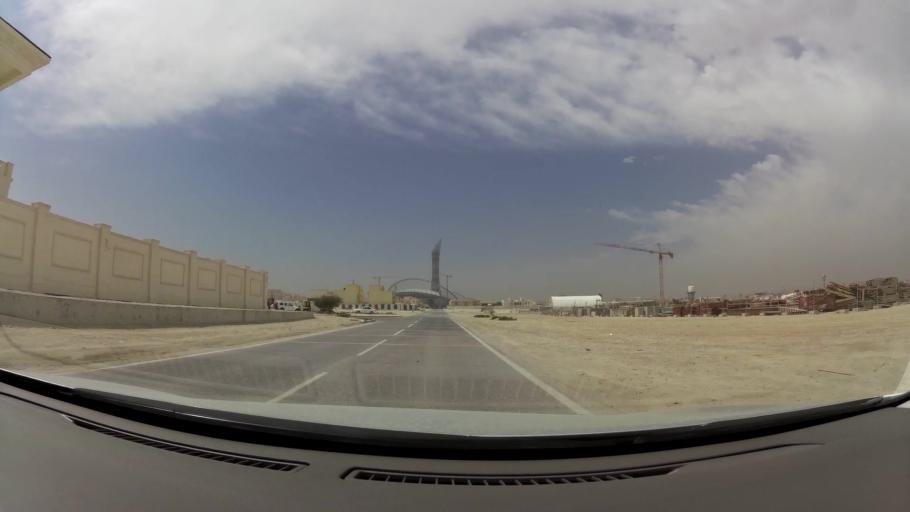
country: QA
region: Baladiyat ar Rayyan
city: Ar Rayyan
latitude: 25.2691
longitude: 51.4610
